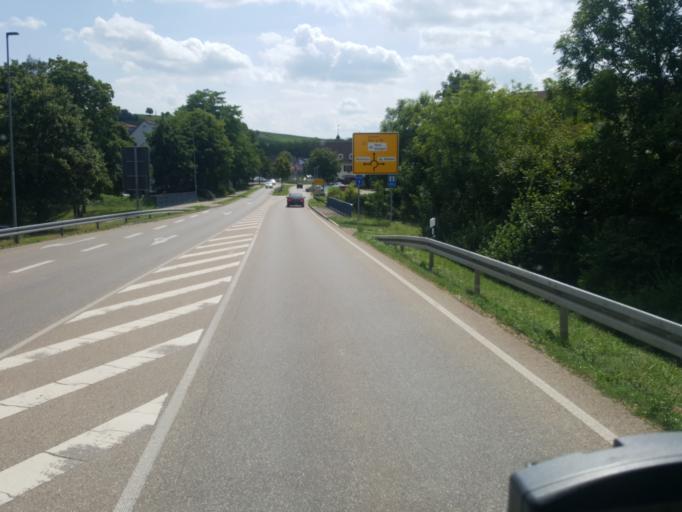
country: DE
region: Baden-Wuerttemberg
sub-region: Freiburg Region
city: Mullheim
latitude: 47.8144
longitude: 7.6110
